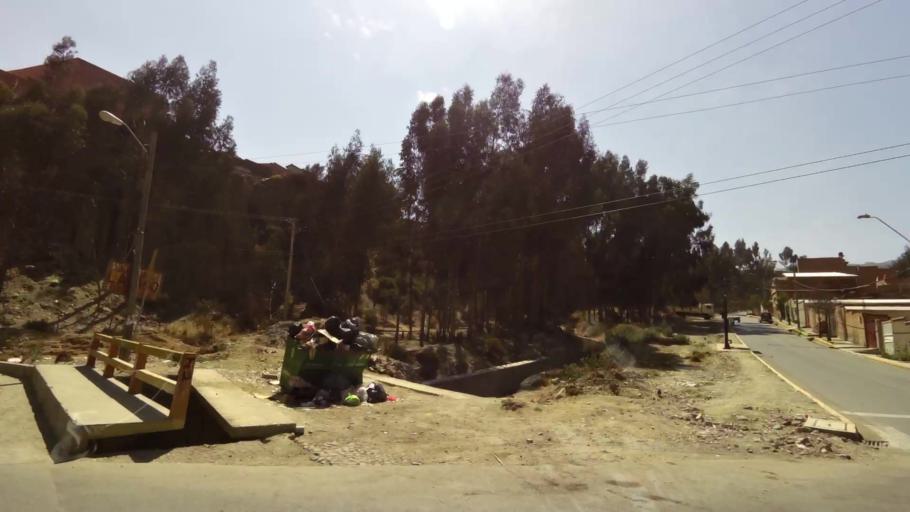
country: BO
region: La Paz
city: La Paz
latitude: -16.5376
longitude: -68.0436
